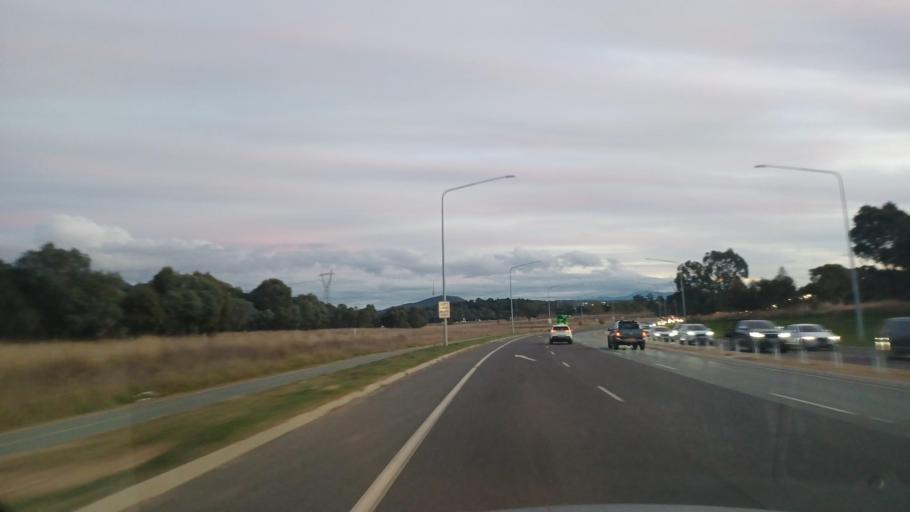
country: AU
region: Australian Capital Territory
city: Kaleen
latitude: -35.2218
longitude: 149.1302
